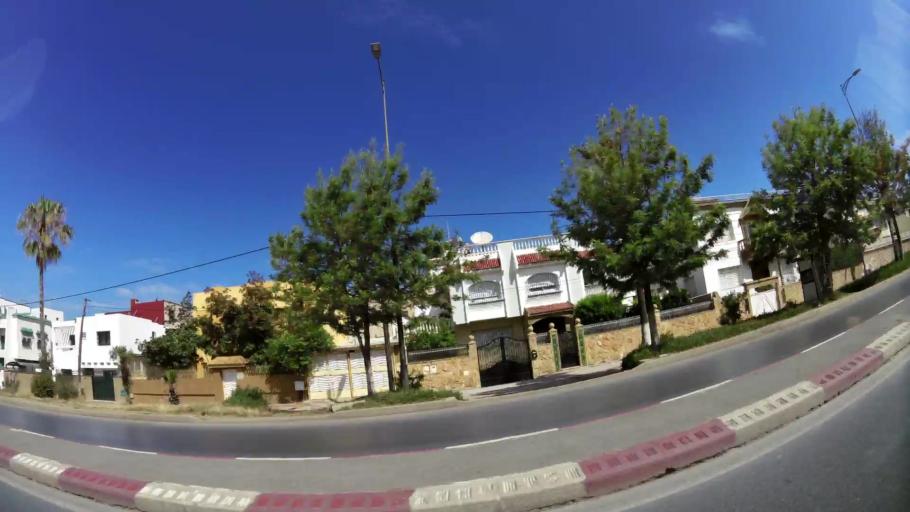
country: MA
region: Rabat-Sale-Zemmour-Zaer
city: Sale
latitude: 34.0653
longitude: -6.7958
